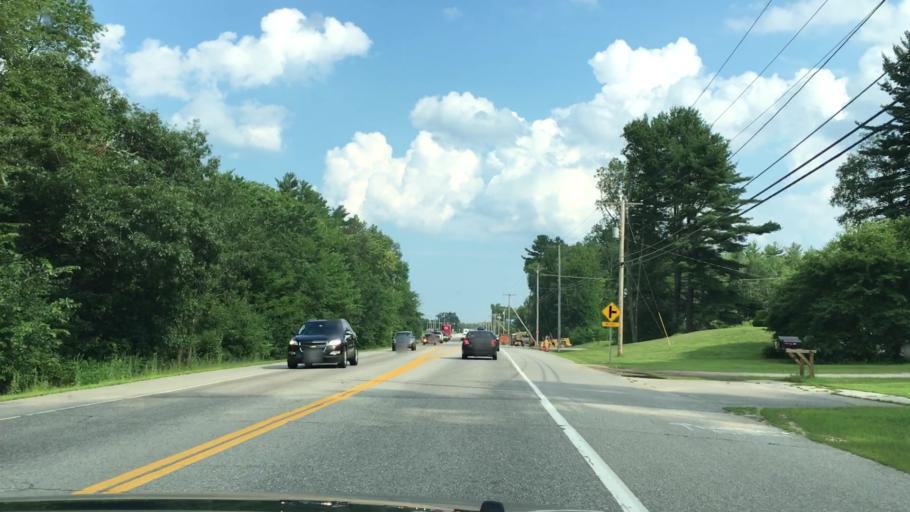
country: US
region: New Hampshire
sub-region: Strafford County
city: Rochester
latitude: 43.3393
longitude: -71.0159
